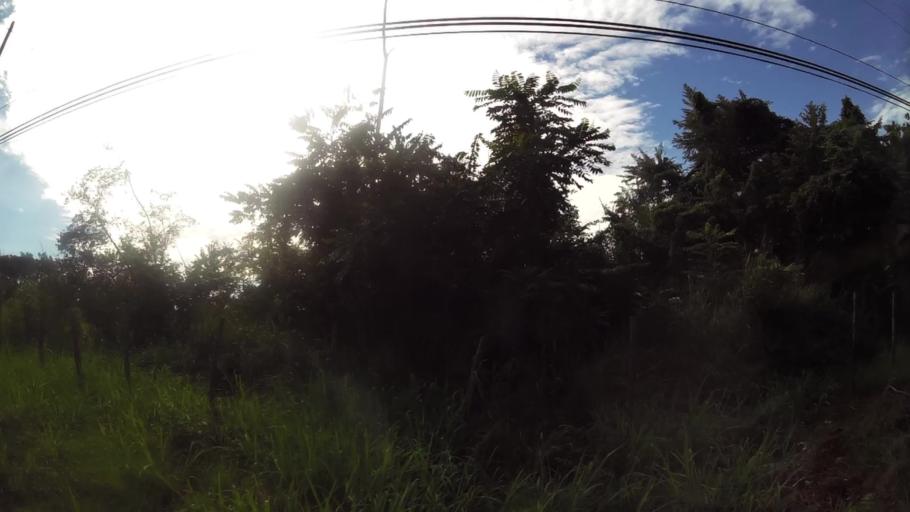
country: PA
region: Panama
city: Nueva Gorgona
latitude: 8.5300
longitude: -79.8840
